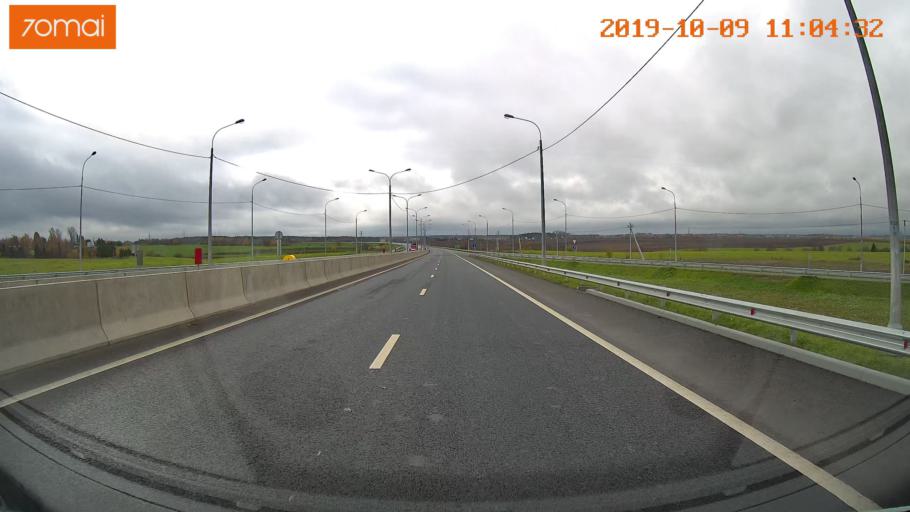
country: RU
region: Vologda
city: Vologda
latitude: 59.2112
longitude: 39.7665
